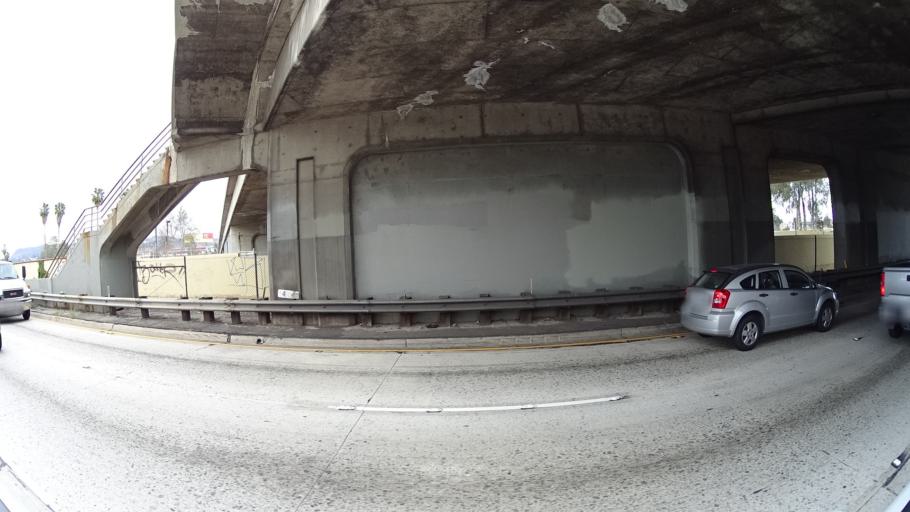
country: US
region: California
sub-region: Los Angeles County
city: Silver Lake
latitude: 34.0795
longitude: -118.2919
